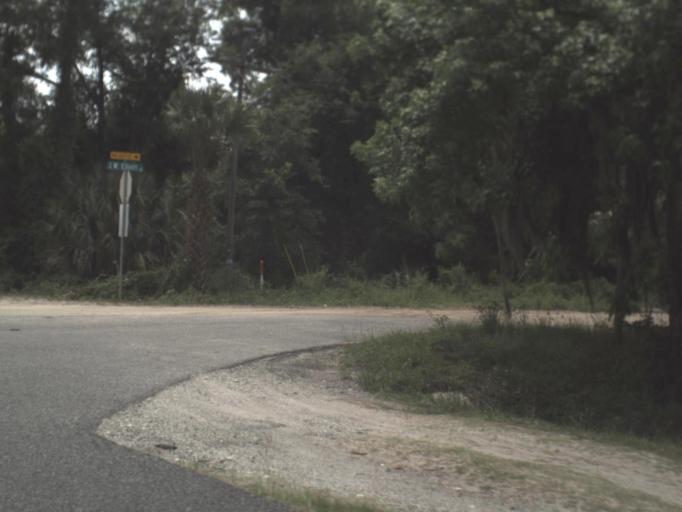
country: US
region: Florida
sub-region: Nassau County
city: Hilliard
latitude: 30.6441
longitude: -81.8692
